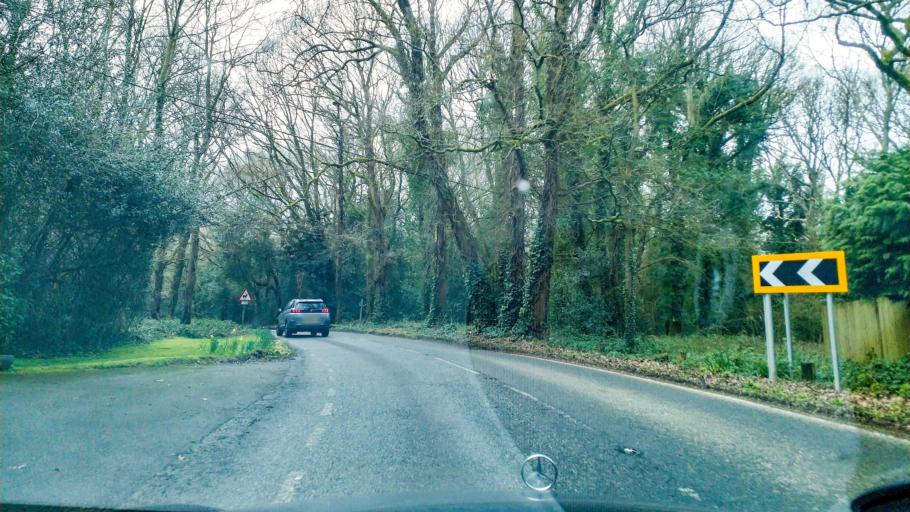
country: GB
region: England
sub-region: Surrey
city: Dorking
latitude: 51.2061
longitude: -0.3067
